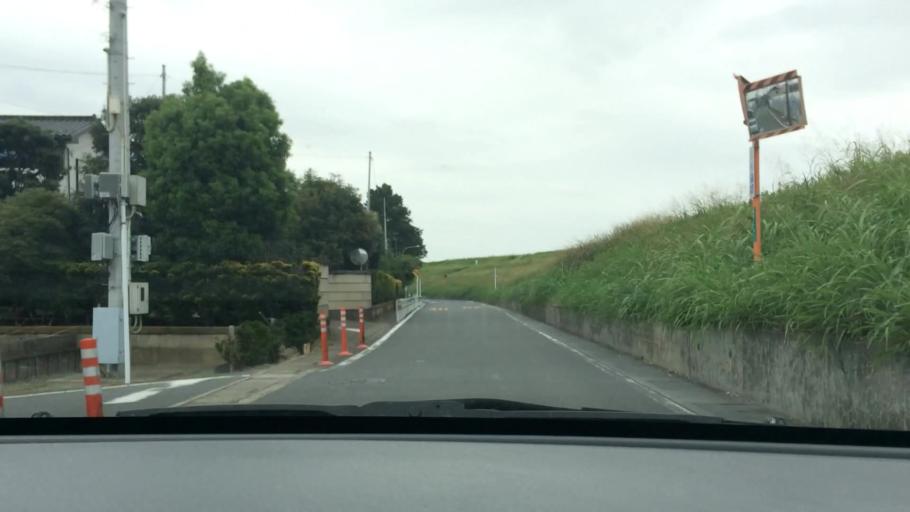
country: JP
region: Chiba
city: Matsudo
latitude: 35.8001
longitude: 139.8891
